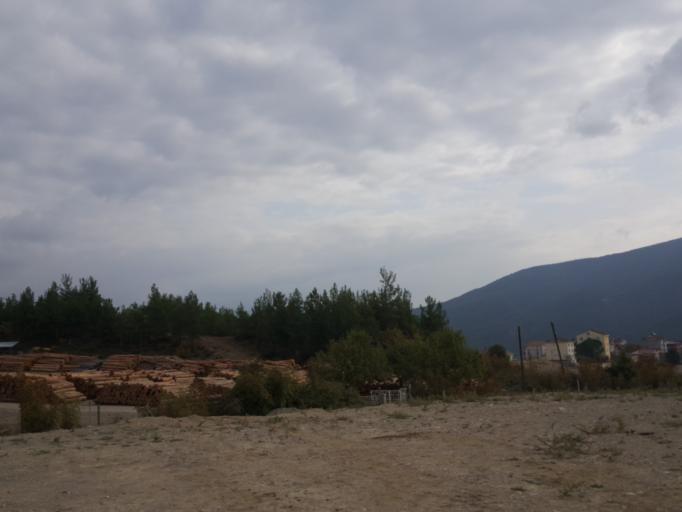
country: TR
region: Sinop
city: Duragan
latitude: 41.4316
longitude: 35.0534
